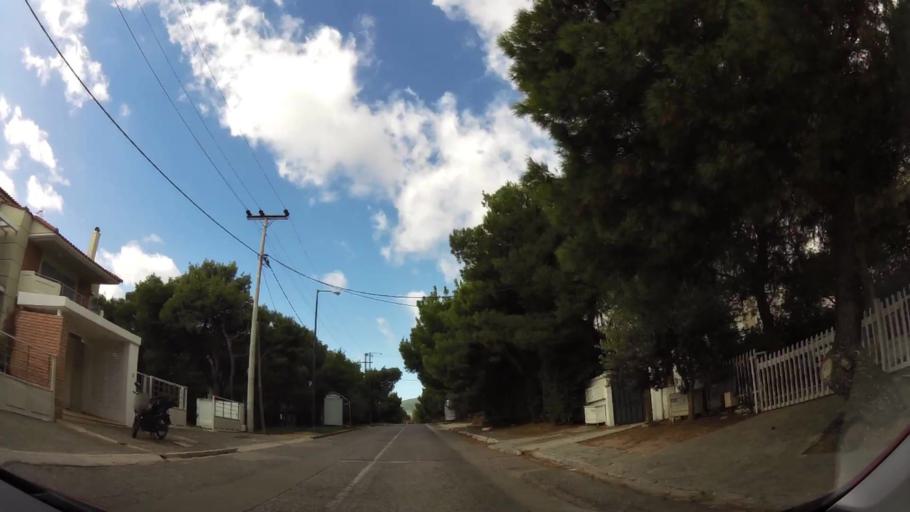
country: GR
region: Attica
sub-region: Nomarchia Anatolikis Attikis
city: Thrakomakedones
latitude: 38.1302
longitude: 23.7620
